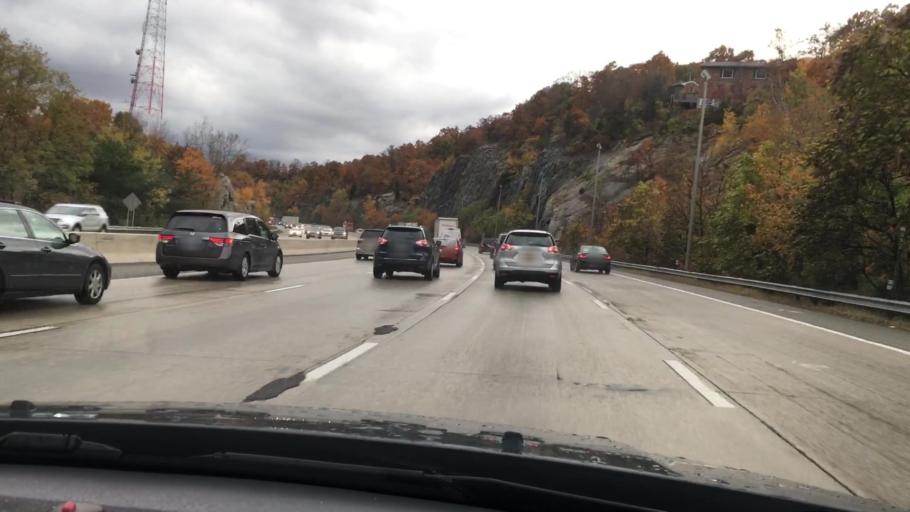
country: US
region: New Jersey
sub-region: Passaic County
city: Pompton Lakes
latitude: 41.0150
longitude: -74.3001
